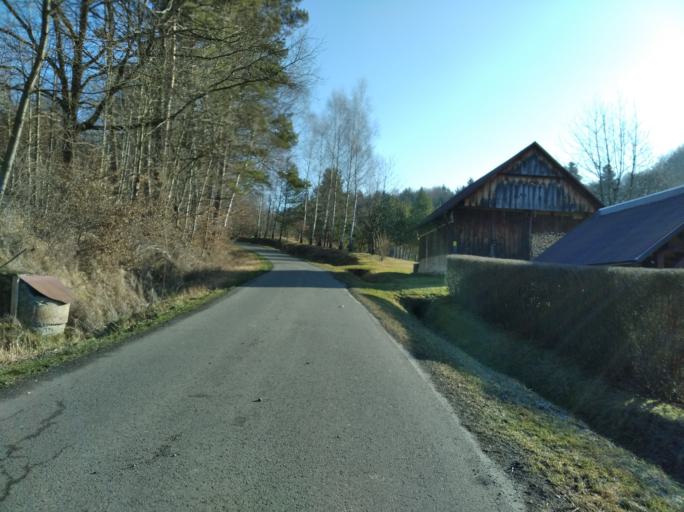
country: PL
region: Subcarpathian Voivodeship
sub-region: Powiat strzyzowski
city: Konieczkowa
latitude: 49.8576
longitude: 21.9322
